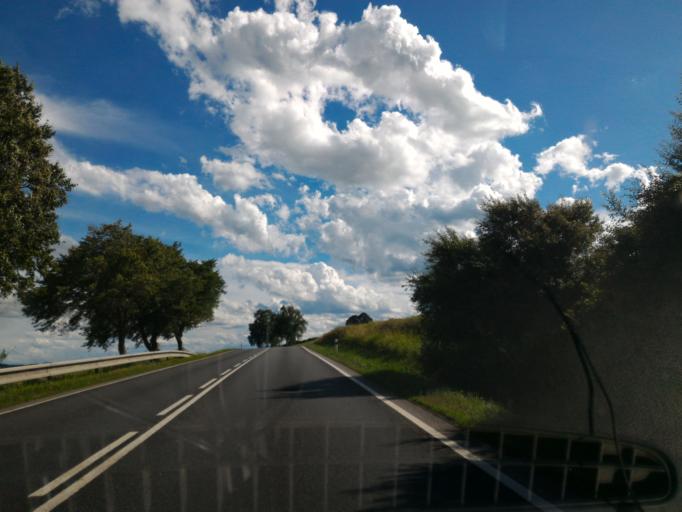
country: CZ
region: Vysocina
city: Dolni Cerekev
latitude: 49.3459
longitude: 15.4842
